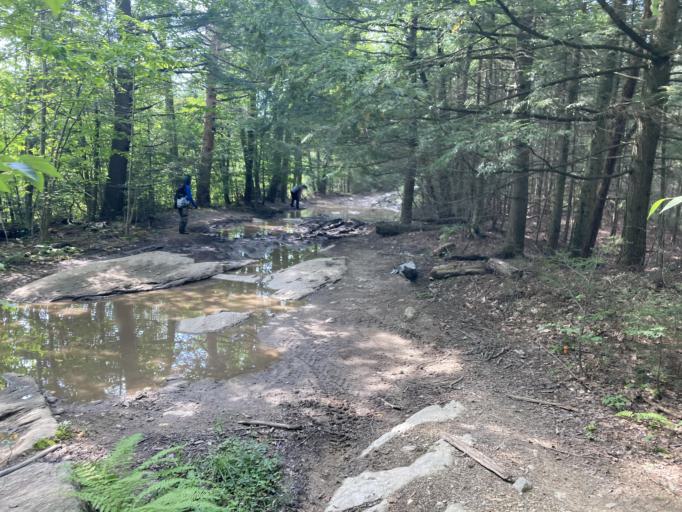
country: US
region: Vermont
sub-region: Franklin County
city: Enosburg Falls
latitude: 44.9623
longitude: -72.9280
